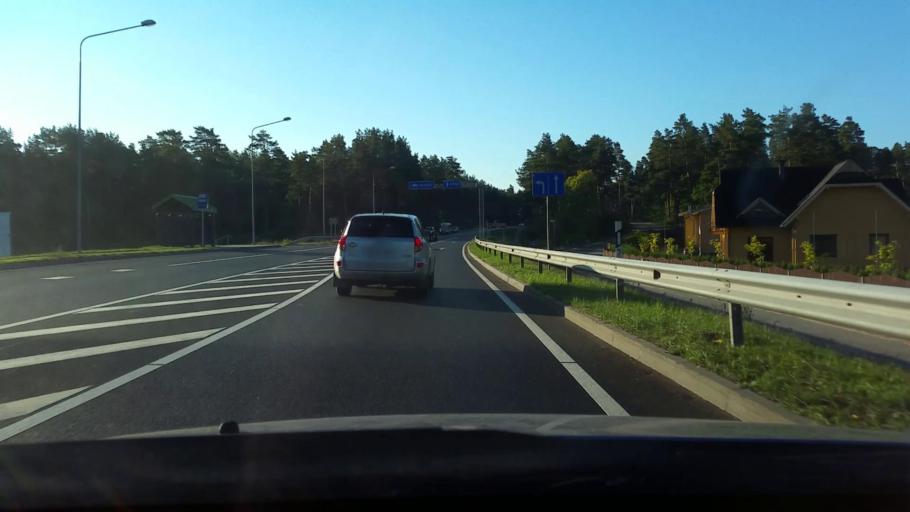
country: LV
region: Adazi
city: Adazi
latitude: 57.0327
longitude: 24.3199
